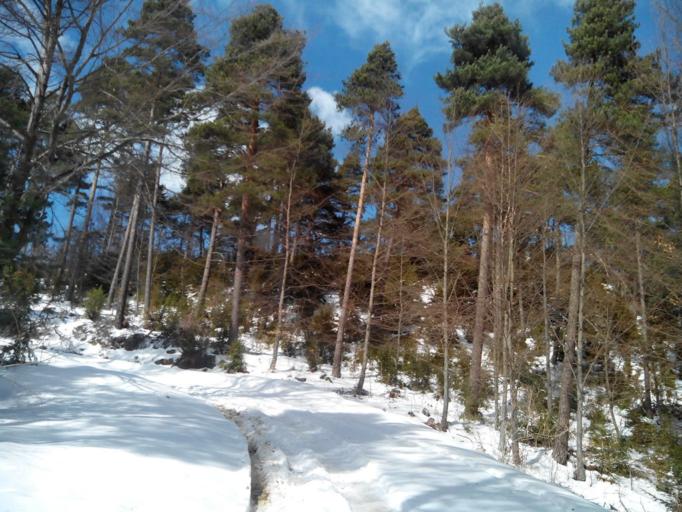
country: ES
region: Catalonia
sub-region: Provincia de Barcelona
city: Sant Julia de Cerdanyola
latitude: 42.2100
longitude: 1.9493
